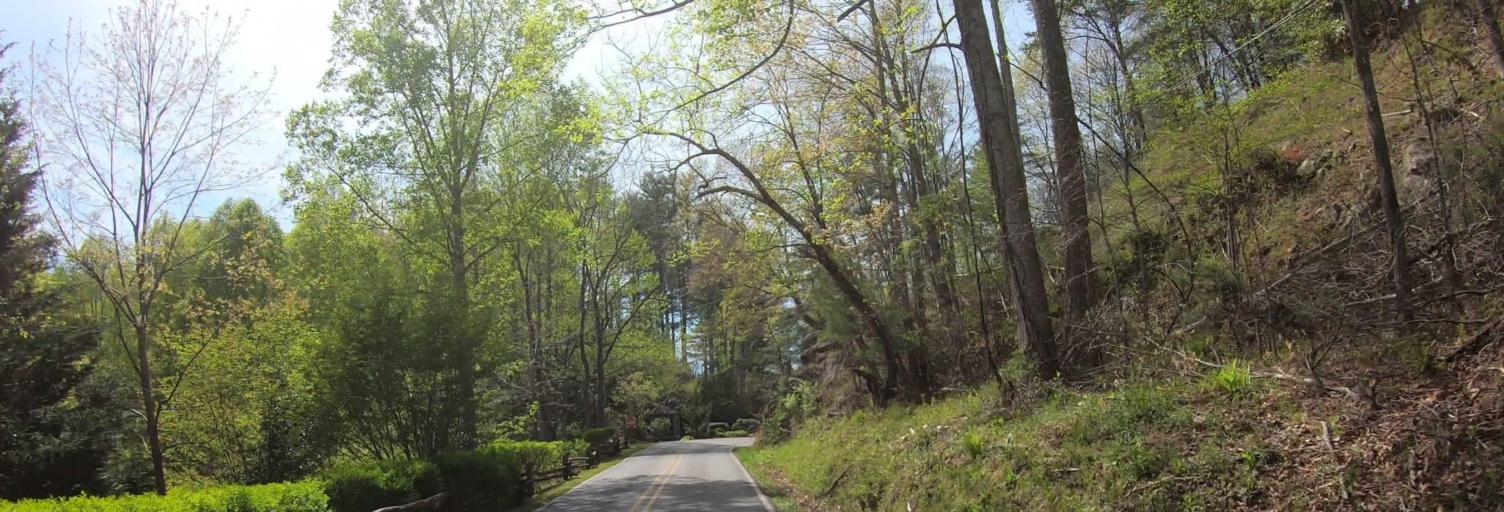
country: US
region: North Carolina
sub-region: Graham County
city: Robbinsville
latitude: 35.3650
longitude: -83.8609
